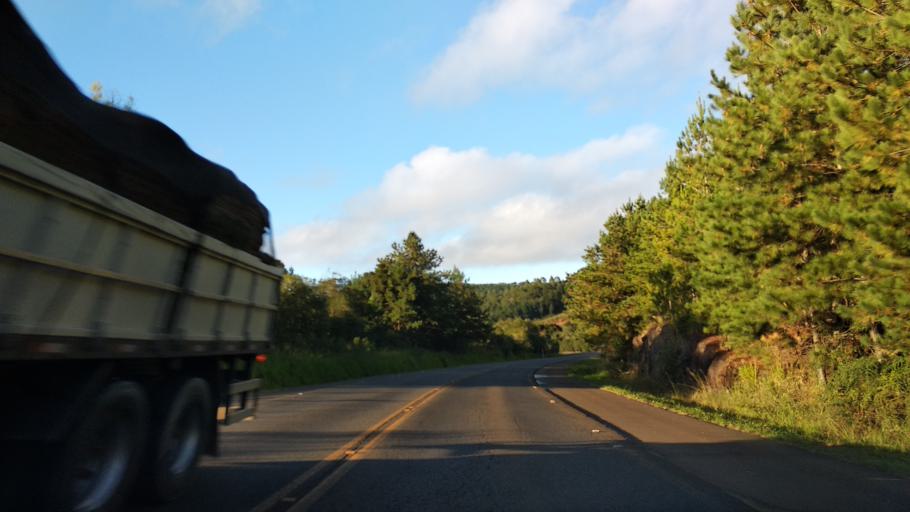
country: BR
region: Santa Catarina
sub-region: Curitibanos
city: Curitibanos
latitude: -27.5902
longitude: -50.7352
